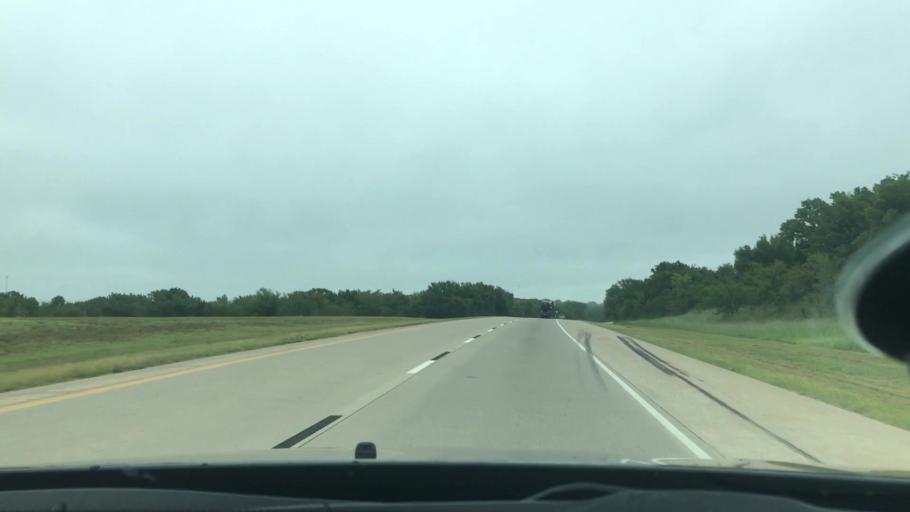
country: US
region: Oklahoma
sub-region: Okmulgee County
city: Henryetta
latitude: 35.4322
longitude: -95.9439
